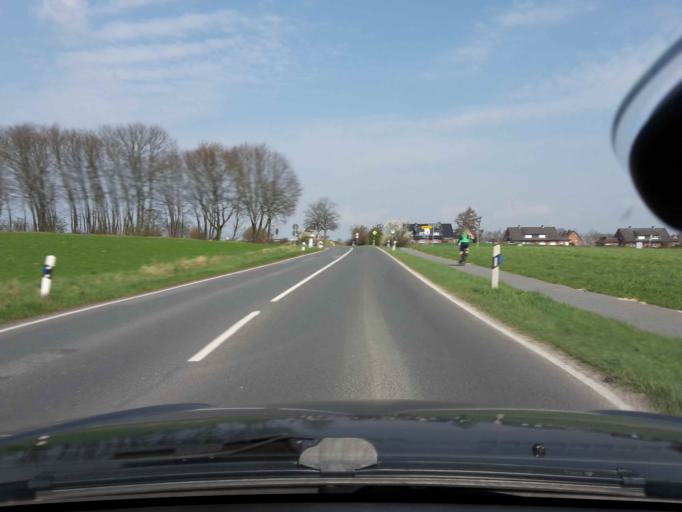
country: DE
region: Lower Saxony
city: Harmstorf
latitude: 53.3719
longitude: 9.9841
